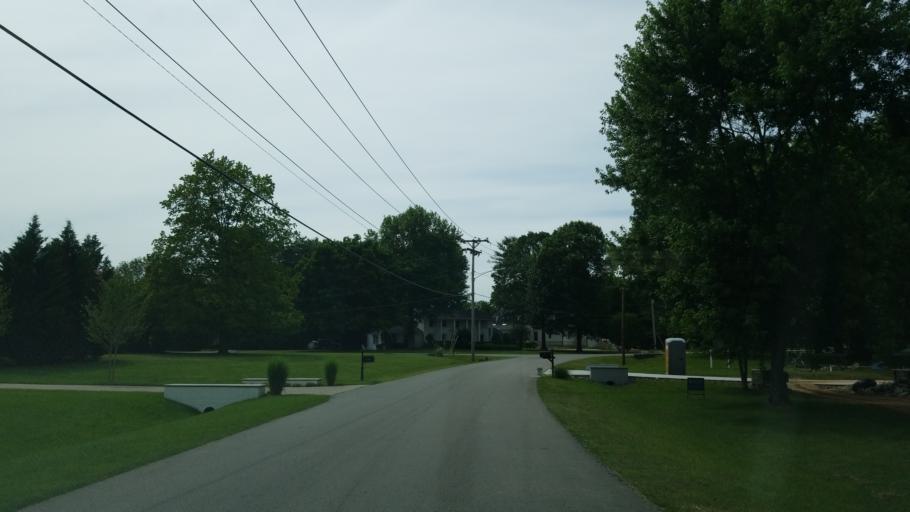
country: US
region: Tennessee
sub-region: Davidson County
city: Forest Hills
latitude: 36.0380
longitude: -86.8299
